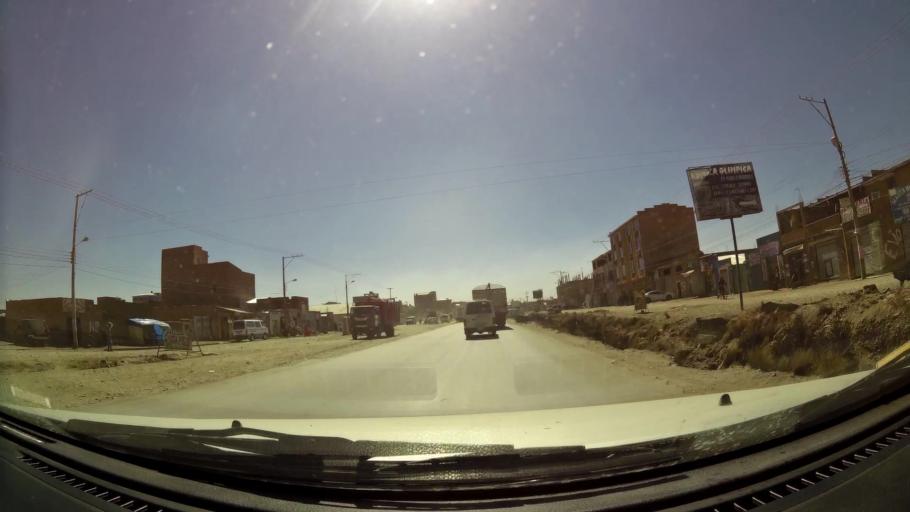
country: BO
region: La Paz
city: La Paz
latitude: -16.5508
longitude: -68.2057
